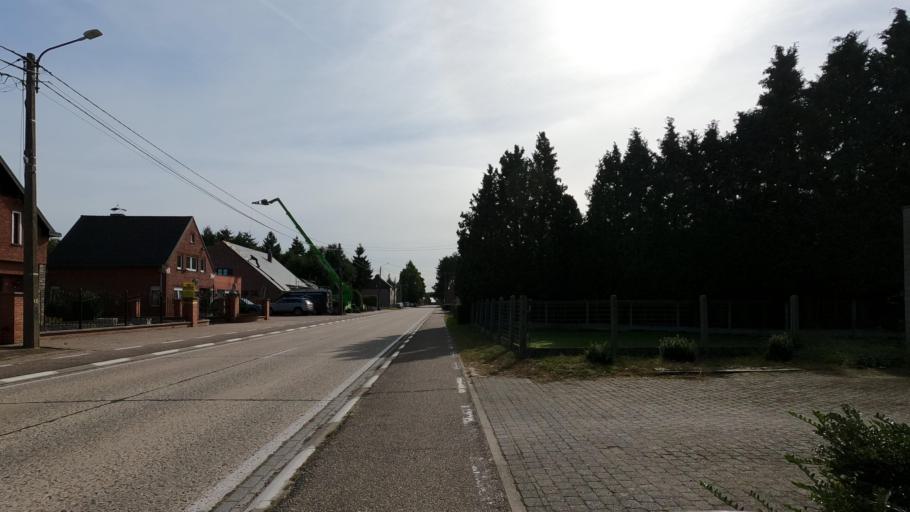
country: BE
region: Flanders
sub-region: Provincie Antwerpen
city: Herselt
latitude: 51.0328
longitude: 4.8914
